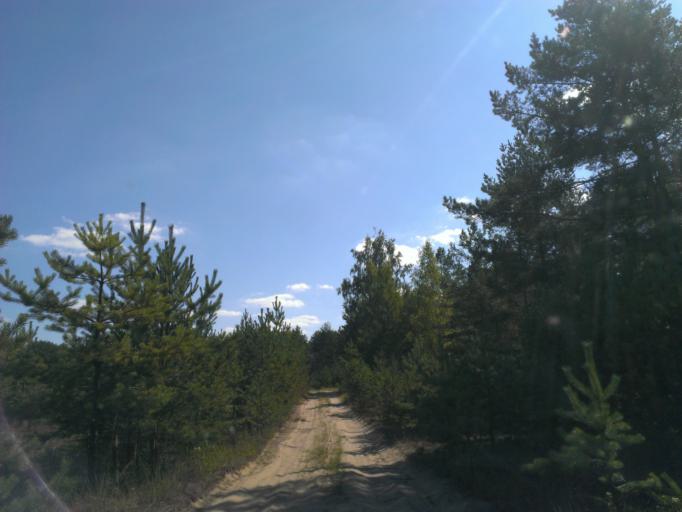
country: LV
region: Adazi
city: Adazi
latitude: 57.1089
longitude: 24.3482
